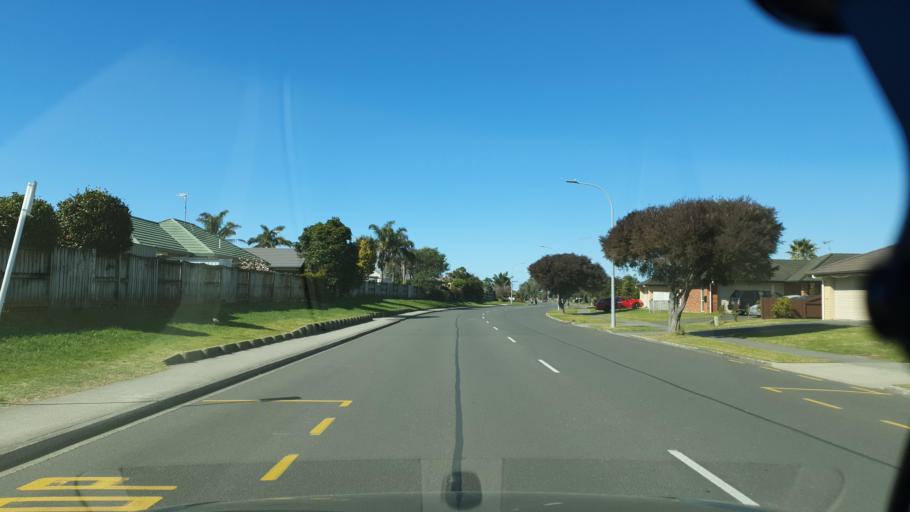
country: NZ
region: Bay of Plenty
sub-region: Tauranga City
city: Tauranga
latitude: -37.7074
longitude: 176.2917
